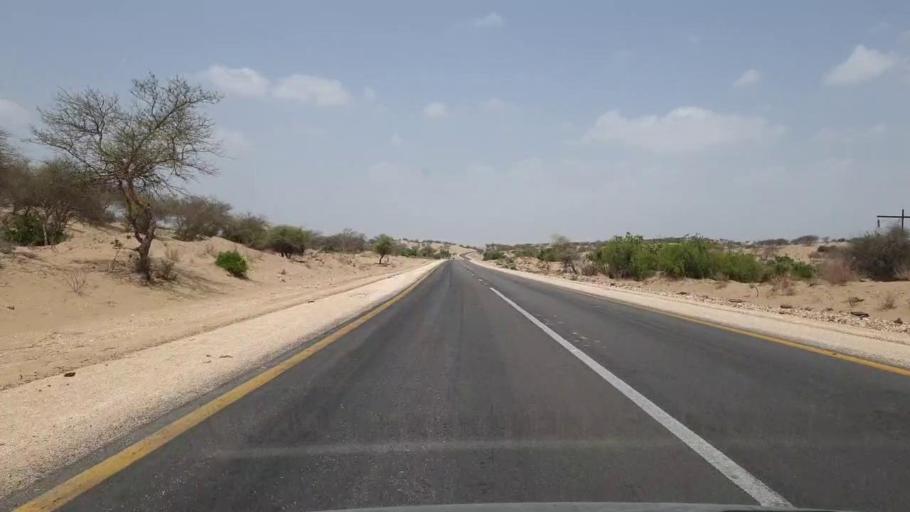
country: PK
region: Sindh
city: Mithi
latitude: 24.8400
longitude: 69.6654
